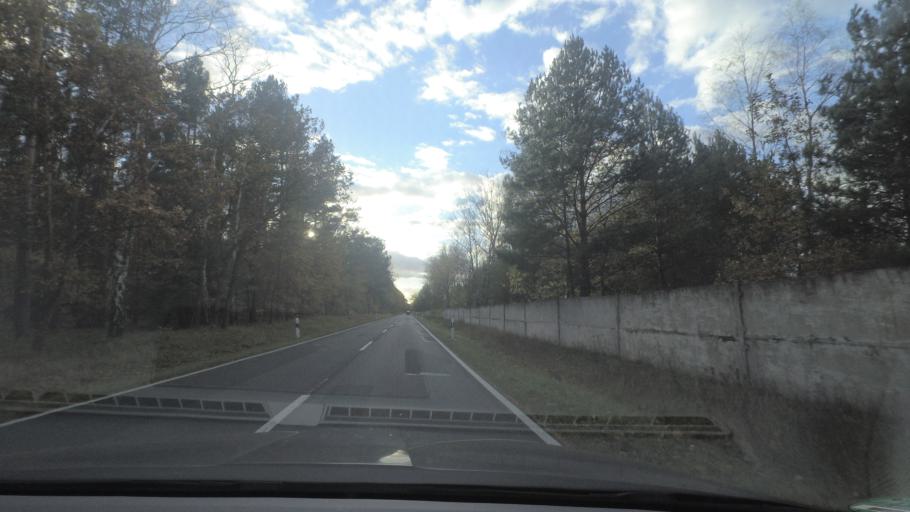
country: DE
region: Brandenburg
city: Sperenberg
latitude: 52.0924
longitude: 13.3570
